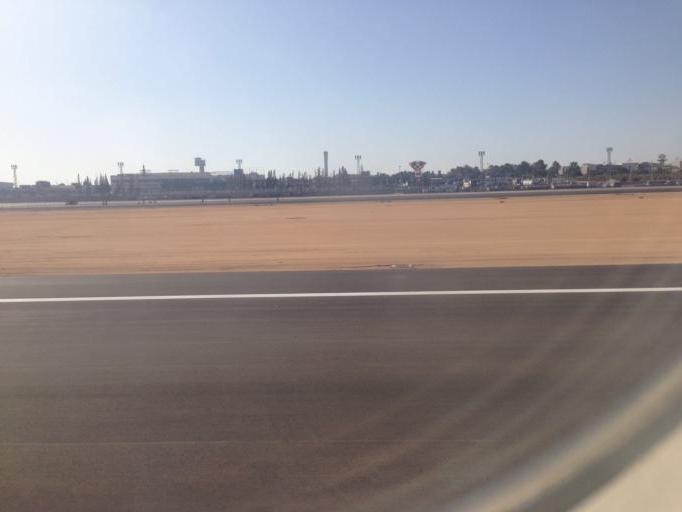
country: EG
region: Muhafazat al Qalyubiyah
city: Al Khankah
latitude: 30.1283
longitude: 31.3915
